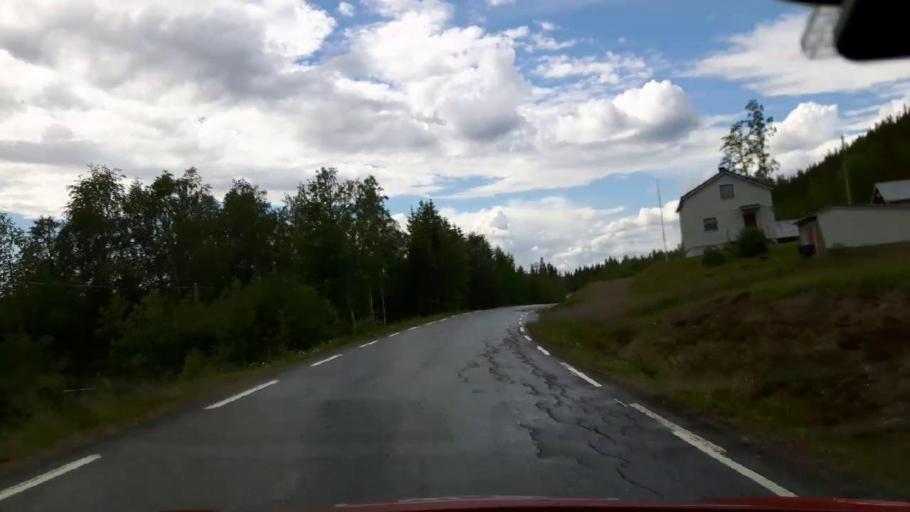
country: NO
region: Nord-Trondelag
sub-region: Lierne
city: Sandvika
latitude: 64.1015
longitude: 14.0061
